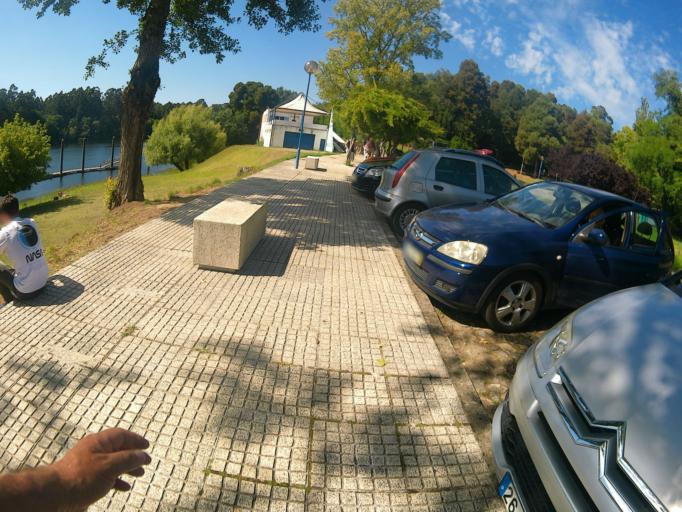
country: PT
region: Viana do Castelo
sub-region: Valenca
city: Valenca
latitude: 42.0236
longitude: -8.6572
